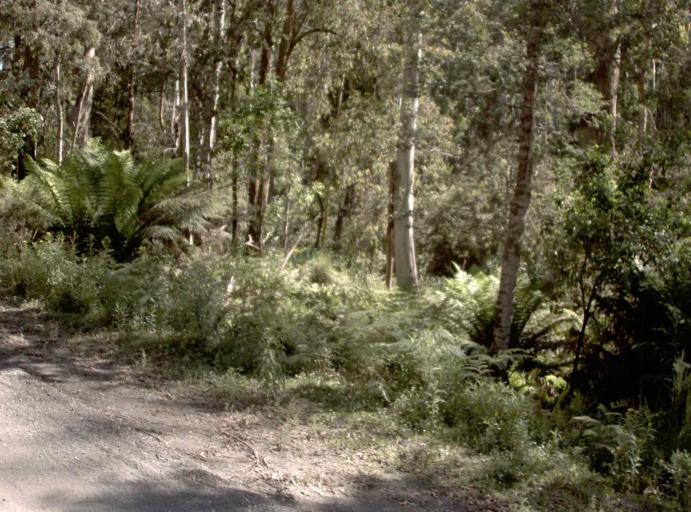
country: AU
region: New South Wales
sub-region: Bombala
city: Bombala
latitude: -37.2222
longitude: 148.7482
